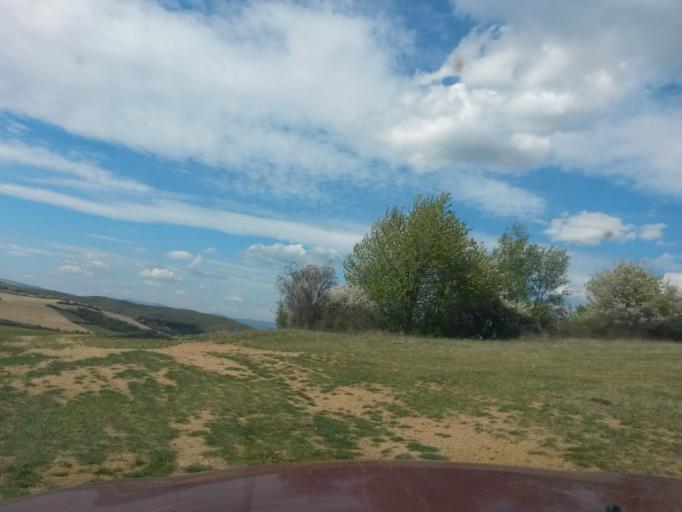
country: SK
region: Presovsky
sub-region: Okres Presov
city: Presov
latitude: 48.9516
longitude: 21.1242
